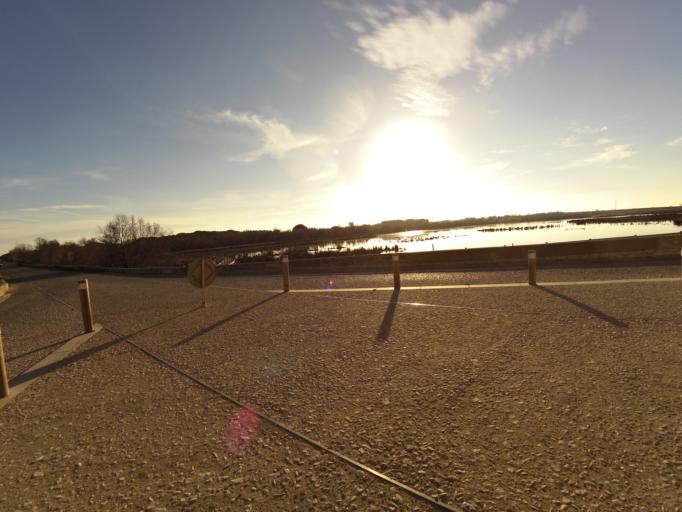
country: FR
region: Languedoc-Roussillon
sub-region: Departement du Gard
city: Aigues-Mortes
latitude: 43.5921
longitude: 4.2095
